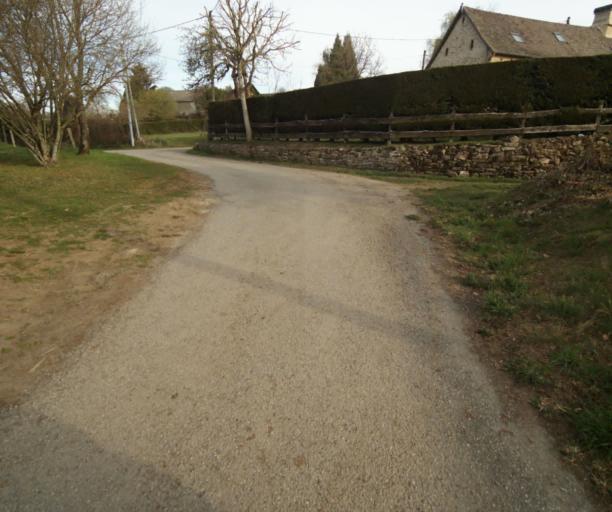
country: FR
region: Limousin
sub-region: Departement de la Correze
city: Chamboulive
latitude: 45.4474
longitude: 1.7779
